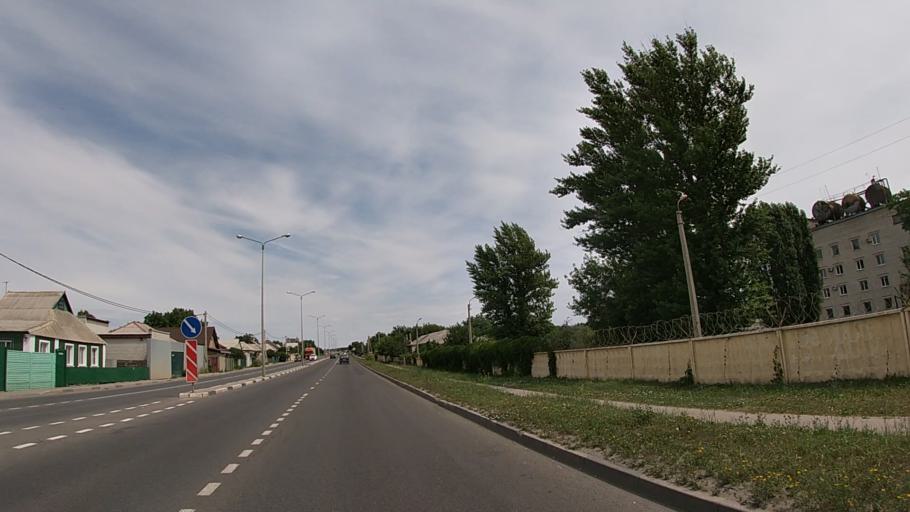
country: RU
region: Belgorod
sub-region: Belgorodskiy Rayon
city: Belgorod
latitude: 50.6198
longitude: 36.5403
